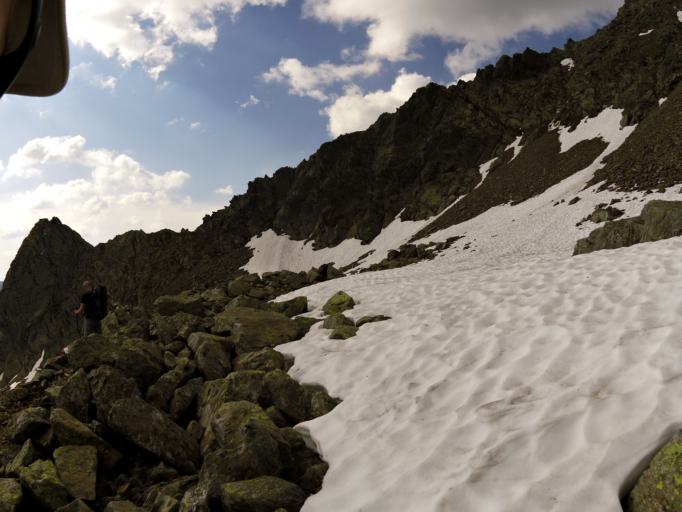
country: AT
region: Tyrol
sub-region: Politischer Bezirk Innsbruck Land
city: Gschnitz
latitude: 47.0387
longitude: 11.3029
